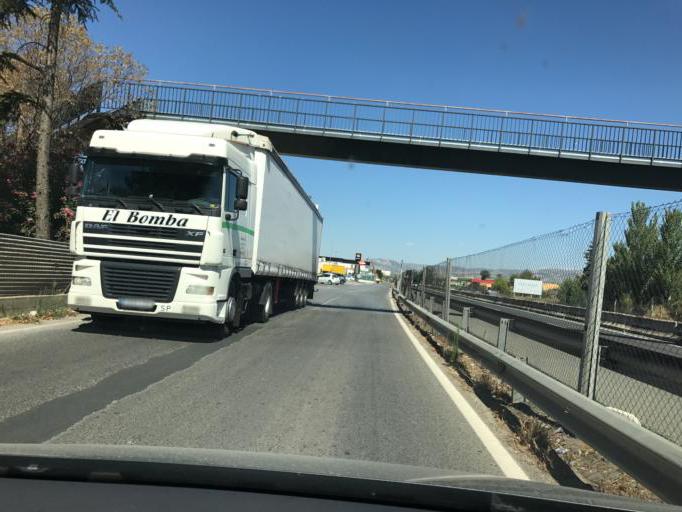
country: ES
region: Andalusia
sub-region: Provincia de Granada
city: Moraleda de Zafayona
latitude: 37.1843
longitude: -3.9571
